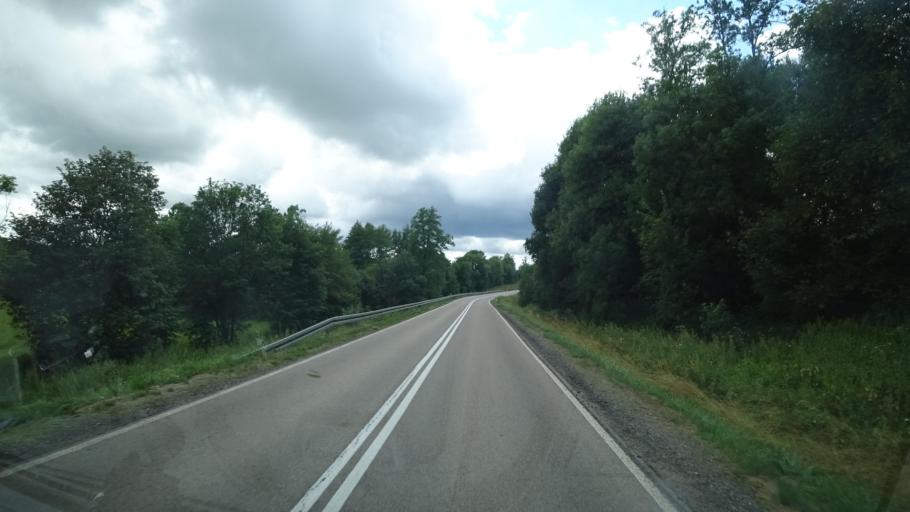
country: PL
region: Warmian-Masurian Voivodeship
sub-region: Powiat goldapski
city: Goldap
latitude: 54.2345
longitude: 22.2533
